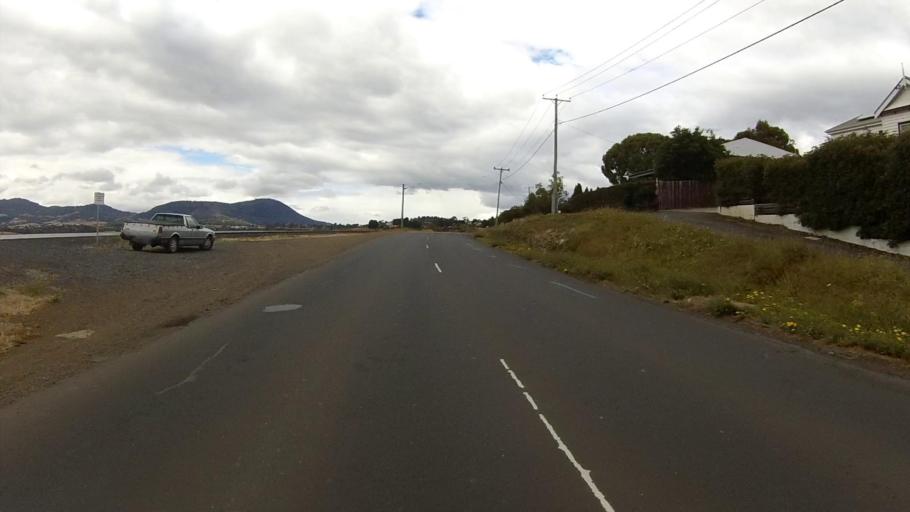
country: AU
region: Tasmania
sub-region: Glenorchy
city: Granton
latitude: -42.7532
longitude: 147.2332
